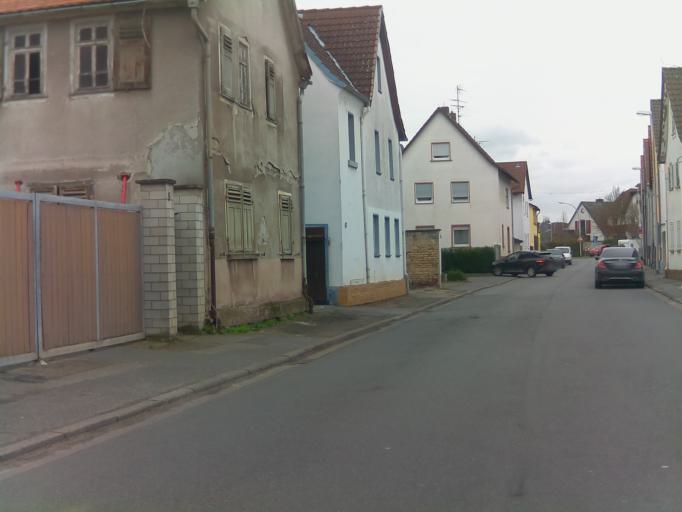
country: DE
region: Hesse
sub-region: Regierungsbezirk Darmstadt
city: Stockstadt am Rhein
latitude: 49.8377
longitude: 8.4635
